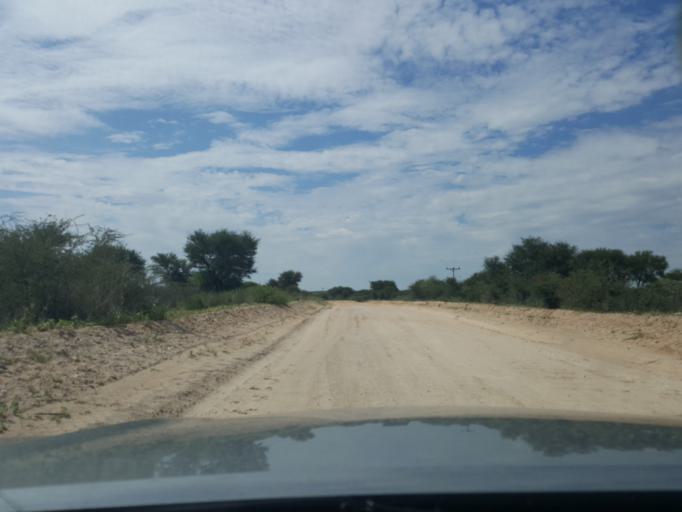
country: BW
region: Kweneng
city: Letlhakeng
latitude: -24.0639
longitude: 25.0308
